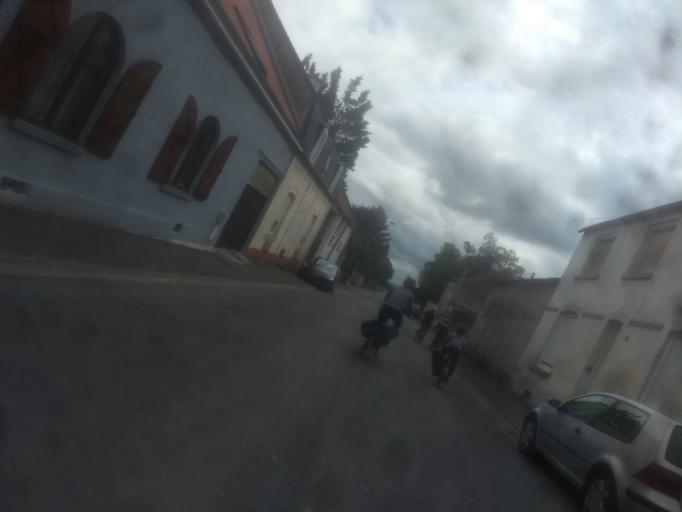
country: FR
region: Nord-Pas-de-Calais
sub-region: Departement du Pas-de-Calais
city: Thelus
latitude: 50.3530
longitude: 2.8001
